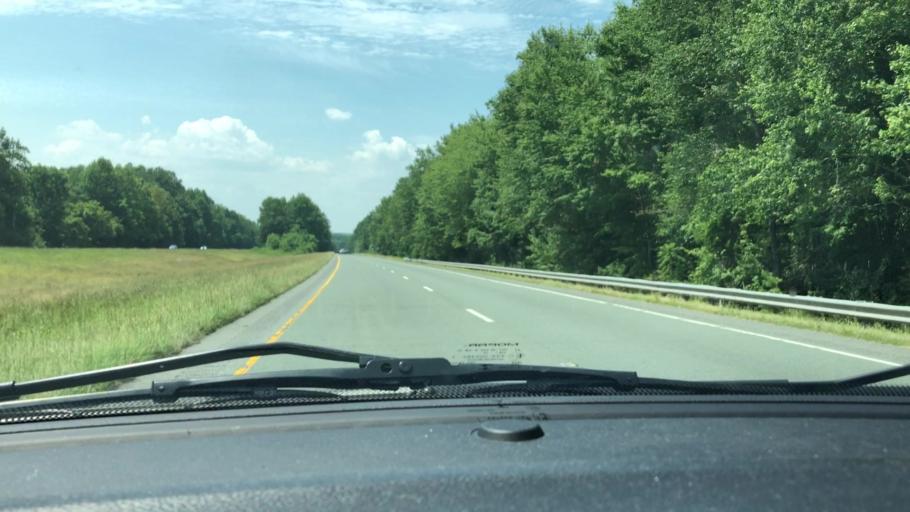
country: US
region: North Carolina
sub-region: Randolph County
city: Liberty
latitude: 35.8549
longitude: -79.6113
